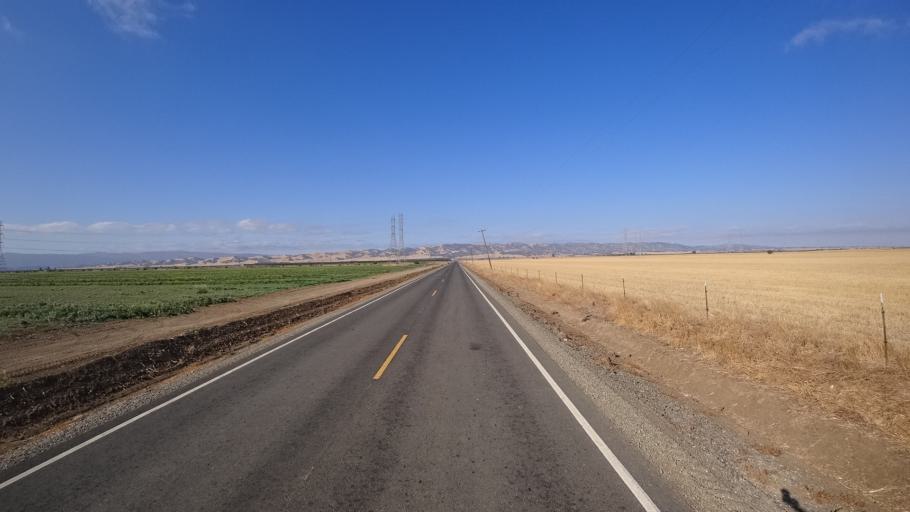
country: US
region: California
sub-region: Yolo County
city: Esparto
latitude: 38.7809
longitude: -122.0121
